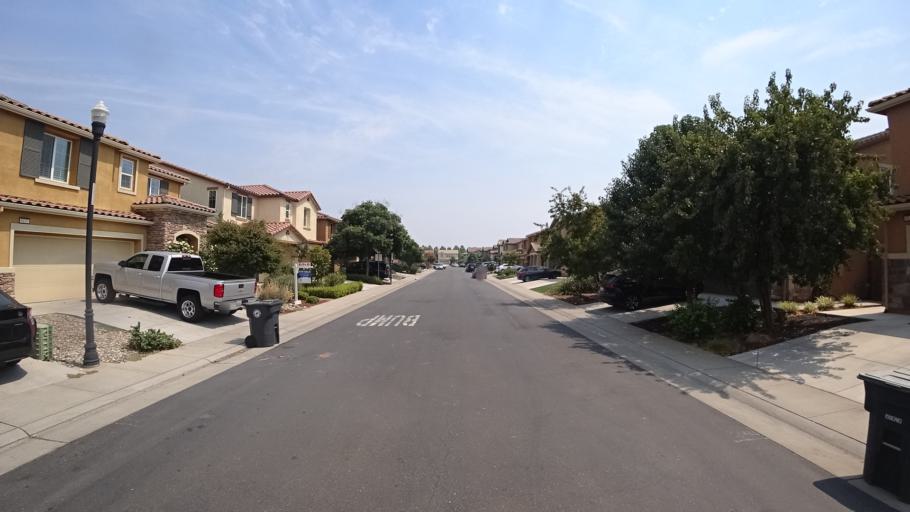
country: US
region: California
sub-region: Sacramento County
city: Laguna
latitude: 38.4038
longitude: -121.4070
